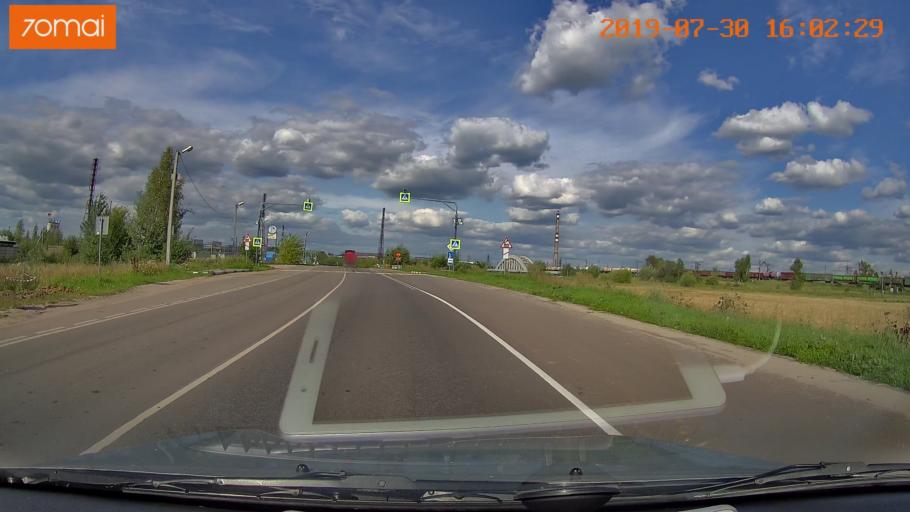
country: RU
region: Moskovskaya
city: Voskresensk
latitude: 55.2882
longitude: 38.6889
